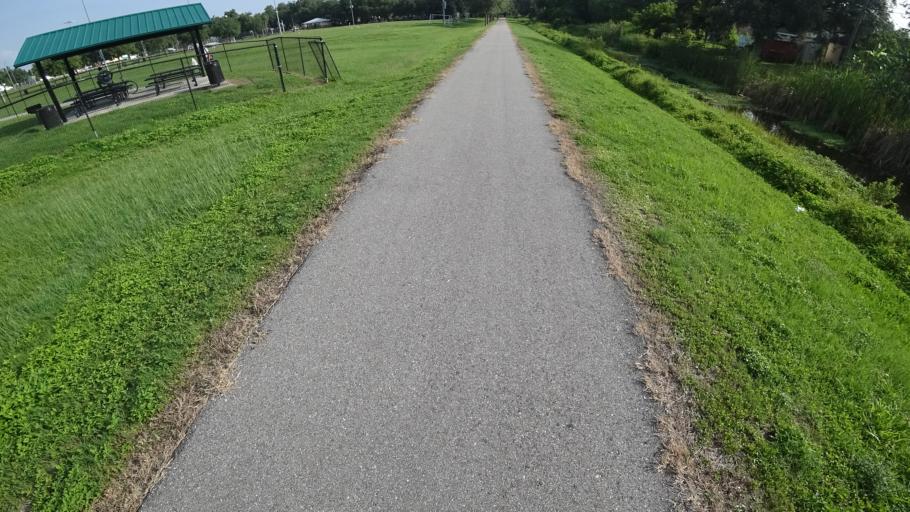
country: US
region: Florida
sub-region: Manatee County
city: Memphis
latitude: 27.5257
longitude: -82.5587
